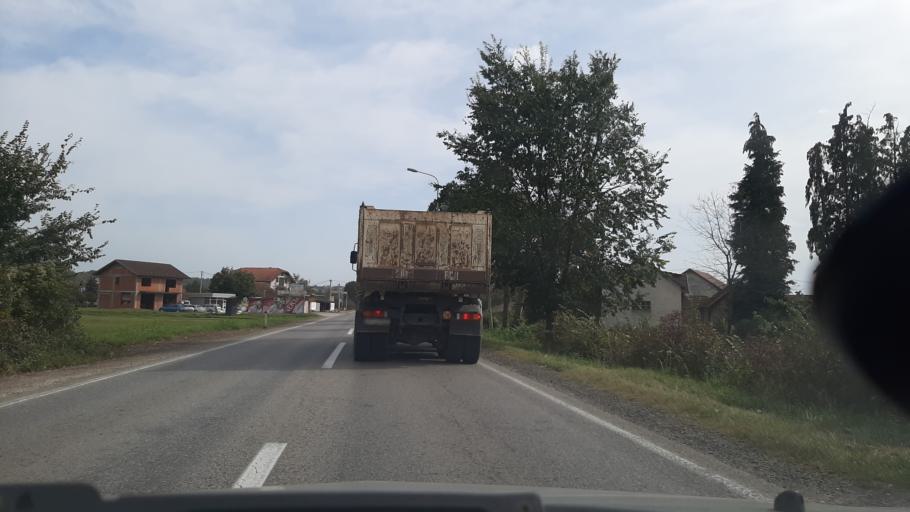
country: BA
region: Republika Srpska
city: Laktasi
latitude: 44.8776
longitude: 17.2963
